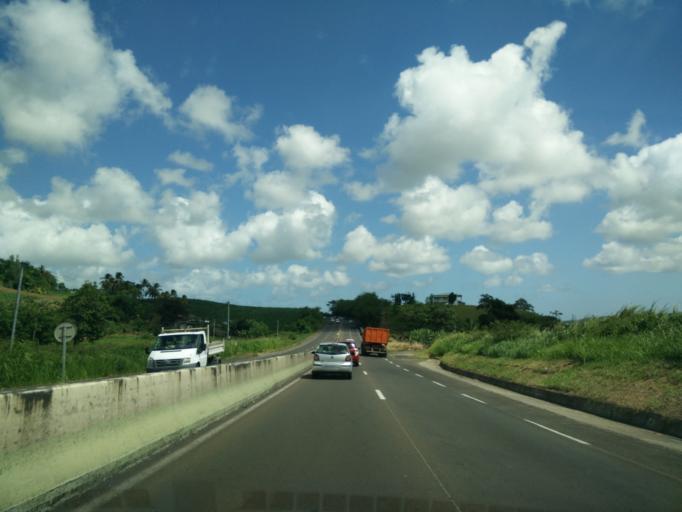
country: MQ
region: Martinique
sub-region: Martinique
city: Ducos
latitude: 14.5666
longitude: -60.9793
